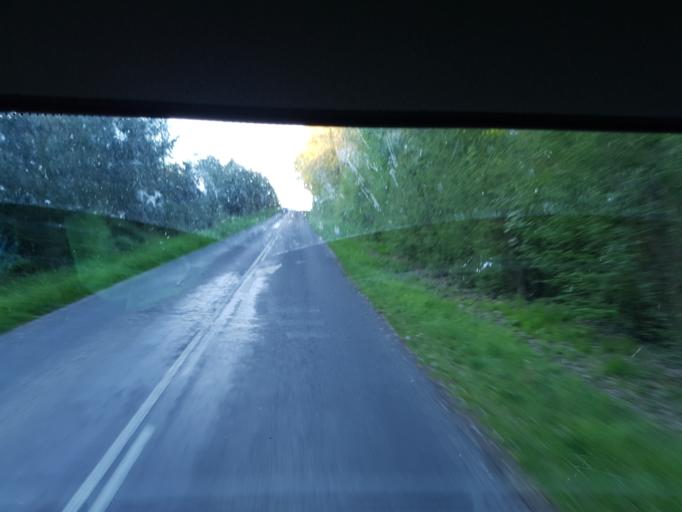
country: FR
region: Champagne-Ardenne
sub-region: Departement de la Marne
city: Esternay
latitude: 48.7042
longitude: 3.5444
